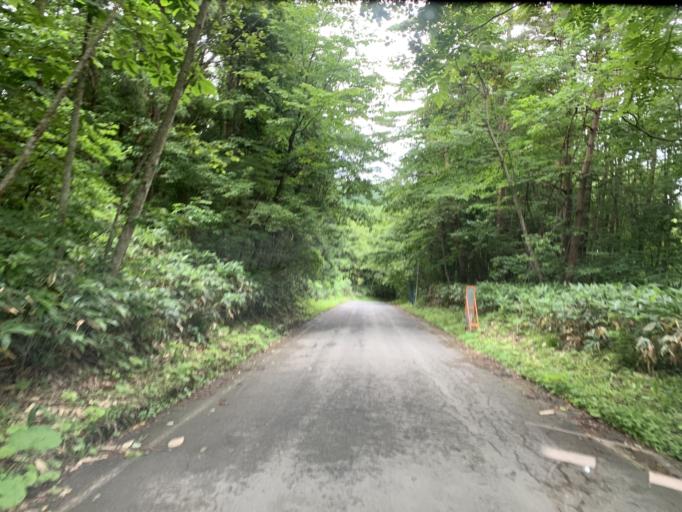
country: JP
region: Iwate
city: Ichinoseki
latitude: 38.9618
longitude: 140.8988
